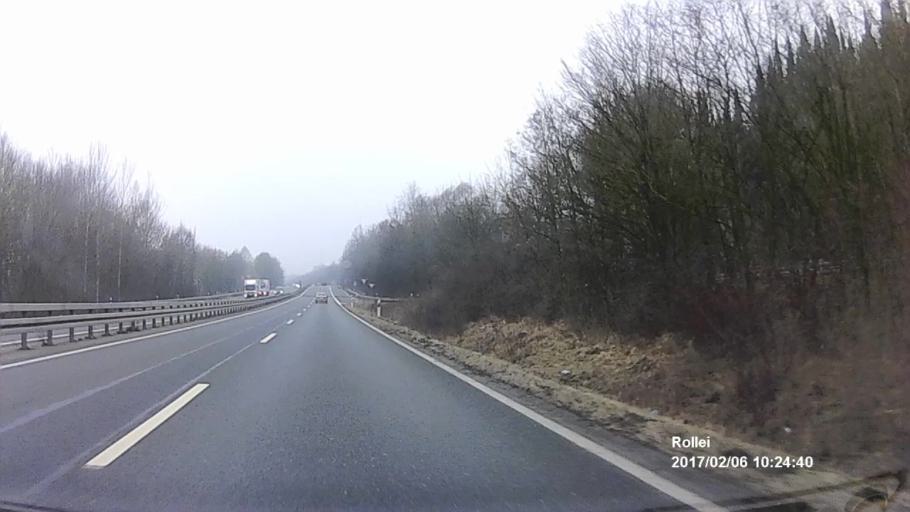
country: DE
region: Lower Saxony
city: Herzberg am Harz
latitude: 51.6348
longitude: 10.3662
